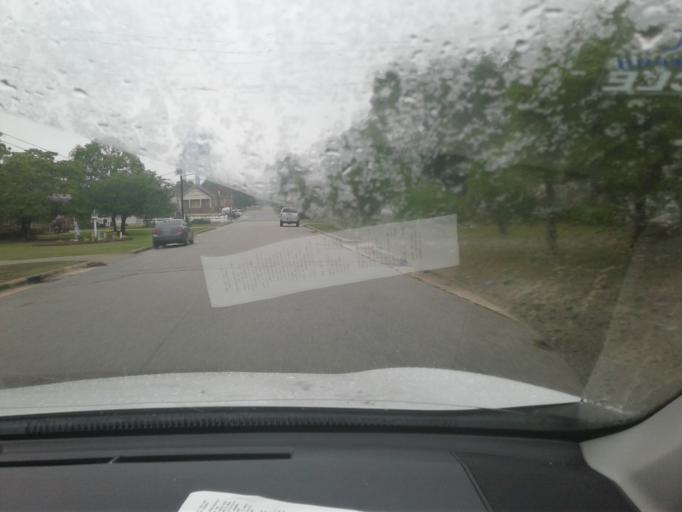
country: US
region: North Carolina
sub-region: Harnett County
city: Erwin
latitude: 35.3232
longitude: -78.6746
